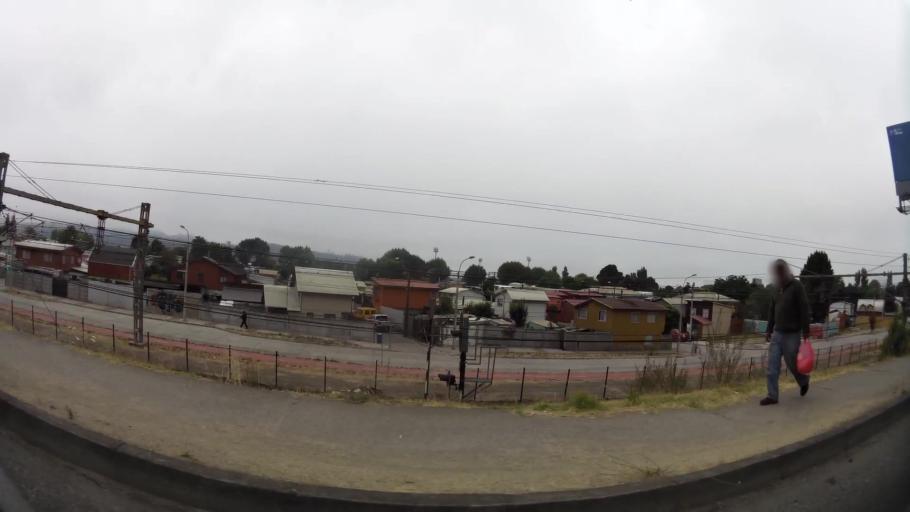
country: CL
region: Biobio
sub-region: Provincia de Concepcion
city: Concepcion
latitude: -36.8381
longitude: -73.0558
